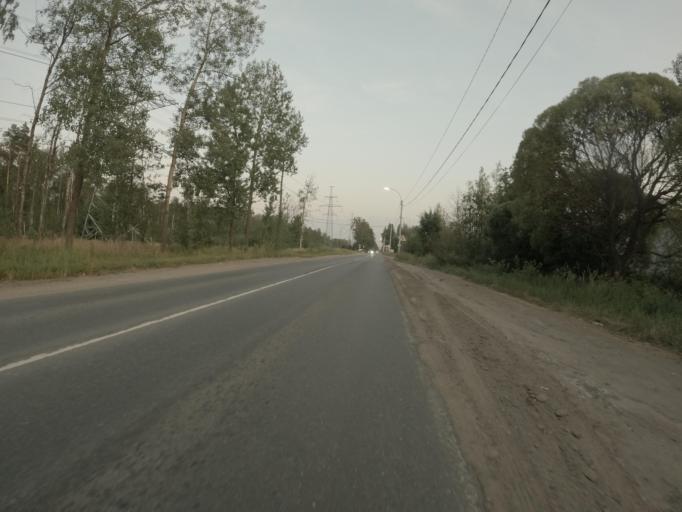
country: RU
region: St.-Petersburg
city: Krasnogvargeisky
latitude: 59.9443
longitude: 30.5209
